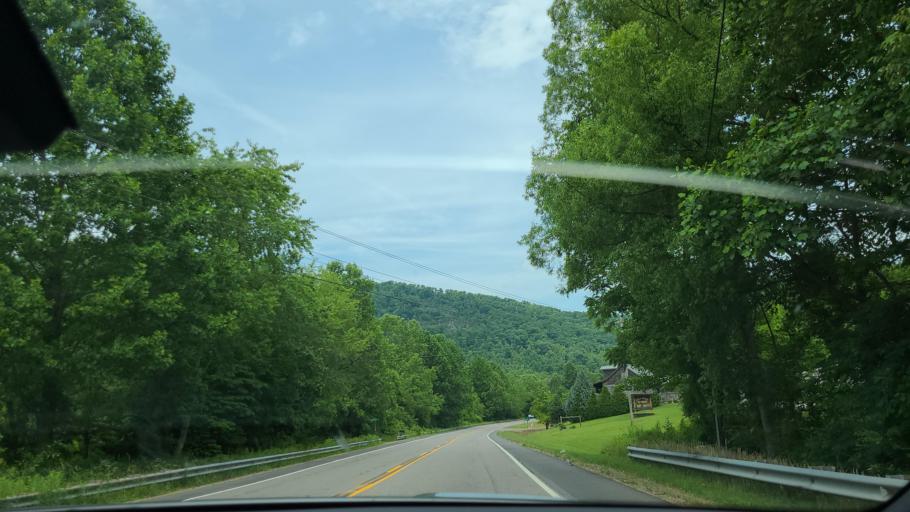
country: US
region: North Carolina
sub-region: Macon County
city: Franklin
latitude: 35.1496
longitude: -83.3123
